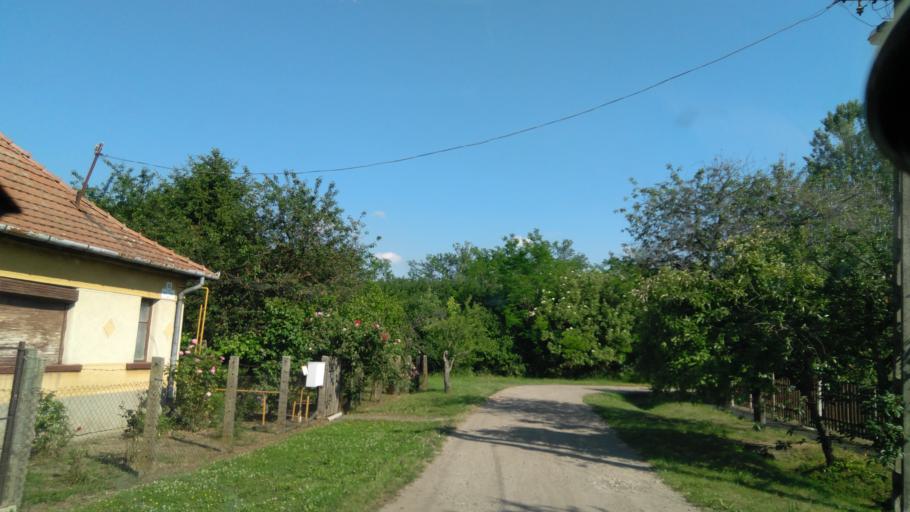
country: HU
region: Bekes
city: Doboz
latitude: 46.7002
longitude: 21.1914
